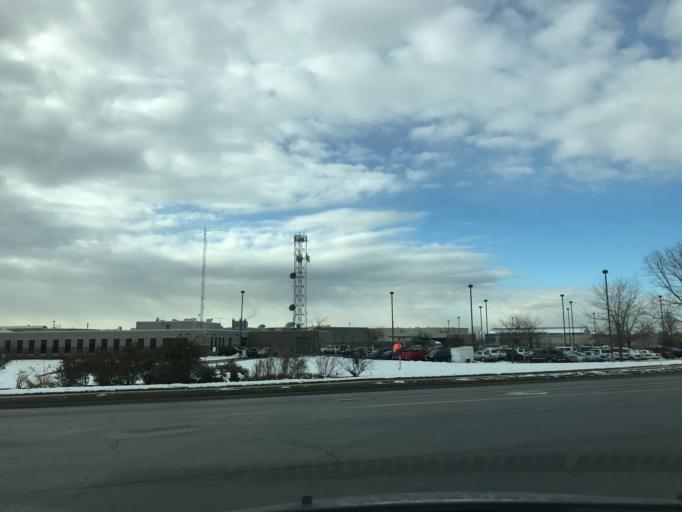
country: US
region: Utah
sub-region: Davis County
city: Farmington
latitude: 40.9822
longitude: -111.9042
